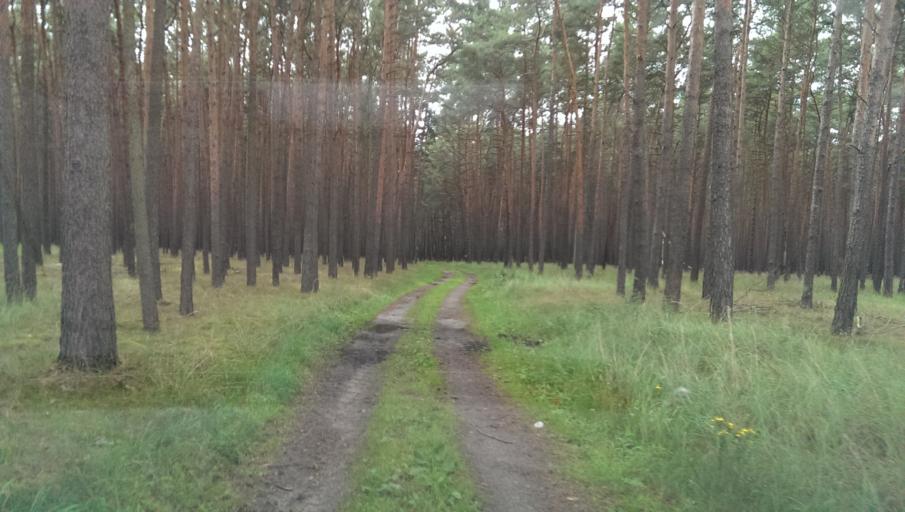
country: DE
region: Brandenburg
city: Linthe
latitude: 52.1509
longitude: 12.7379
